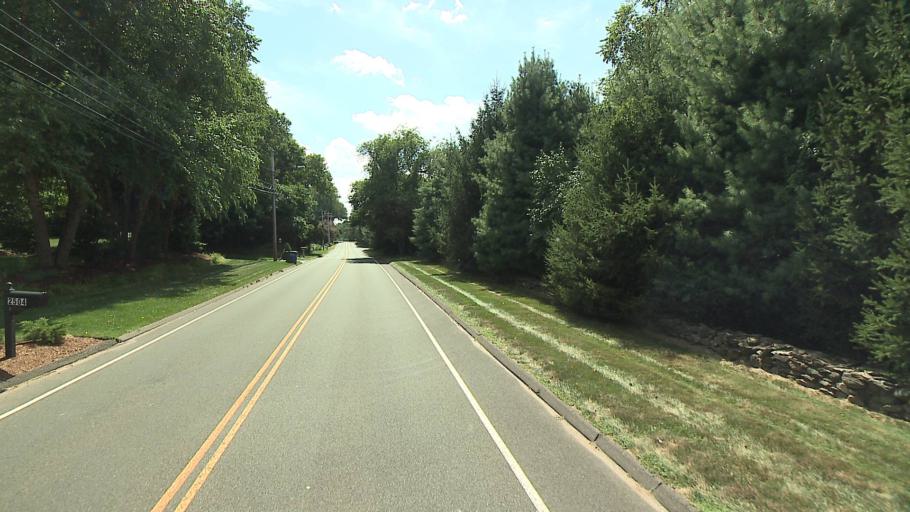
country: US
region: Connecticut
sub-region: Fairfield County
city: Trumbull
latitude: 41.2666
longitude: -73.1660
